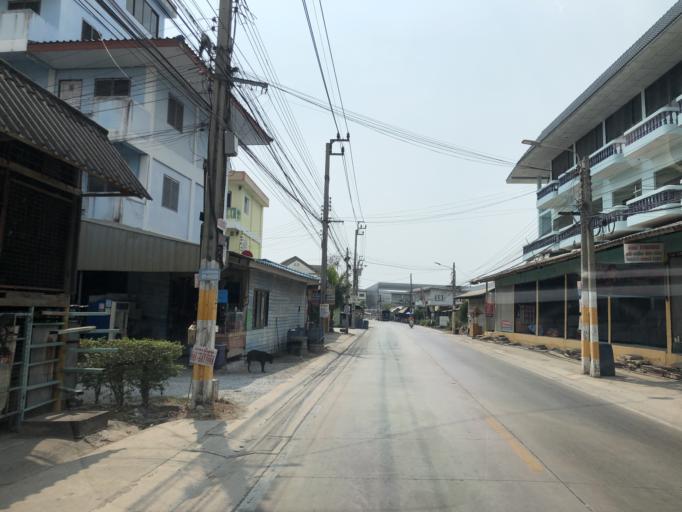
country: TH
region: Samut Prakan
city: Bang Bo
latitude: 13.5720
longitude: 100.8927
